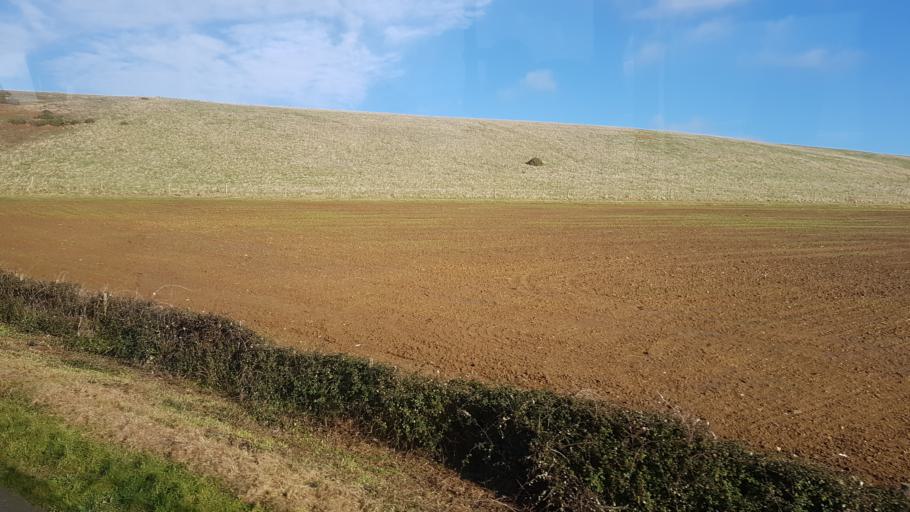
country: GB
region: England
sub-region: Isle of Wight
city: Freshwater
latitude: 50.6605
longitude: -1.4710
